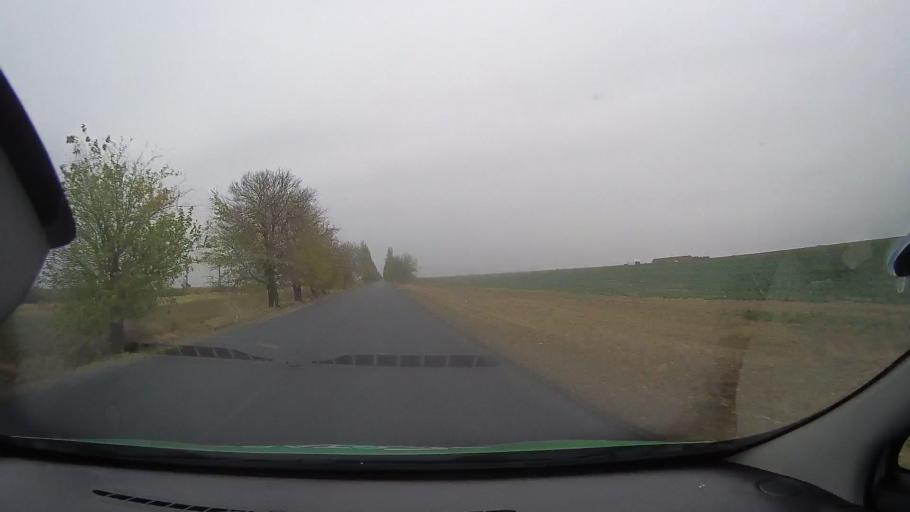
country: RO
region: Ialomita
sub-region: Comuna Valea Ciorii
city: Valea Ciorii
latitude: 44.7072
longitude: 27.5941
